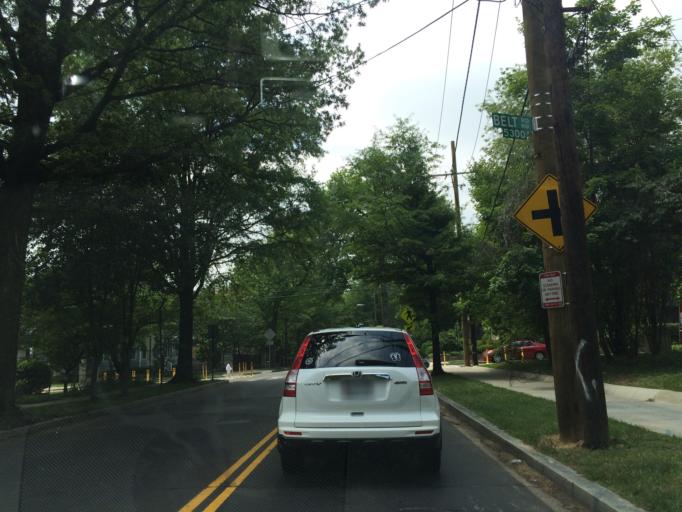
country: US
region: Maryland
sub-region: Montgomery County
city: Friendship Village
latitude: 38.9611
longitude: -77.0816
